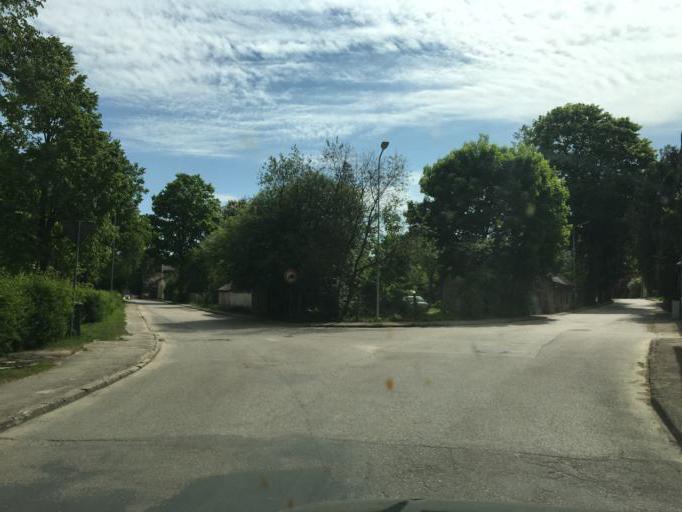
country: LV
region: Talsu Rajons
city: Valdemarpils
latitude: 57.3732
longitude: 22.5862
